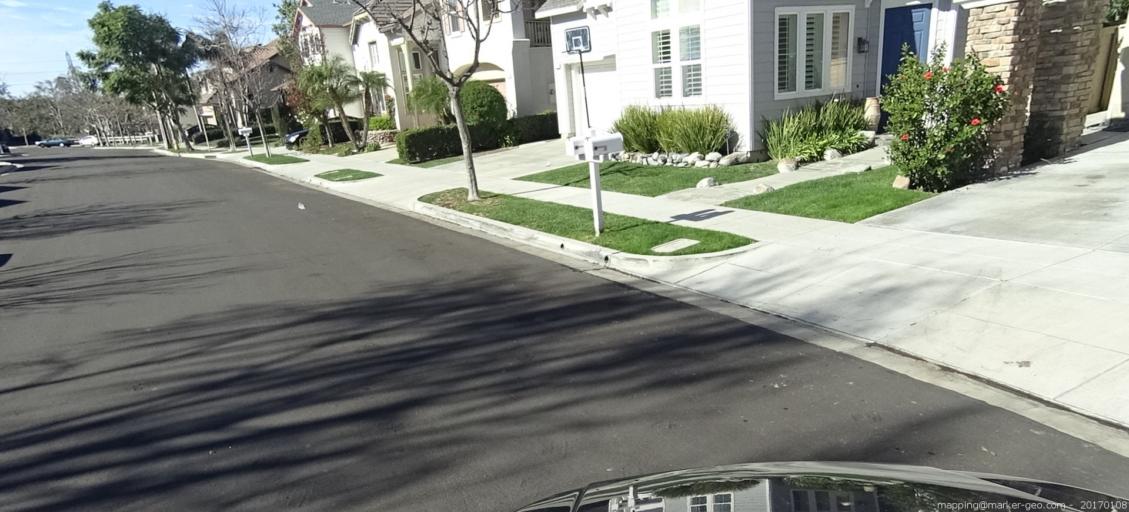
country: US
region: California
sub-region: Orange County
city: Ladera Ranch
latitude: 33.5682
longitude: -117.6386
